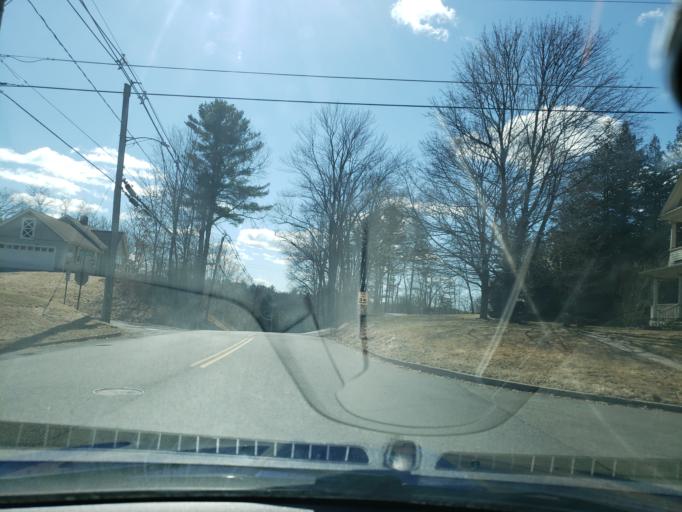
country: US
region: Connecticut
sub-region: Hartford County
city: Hazardville
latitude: 41.9854
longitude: -72.5398
